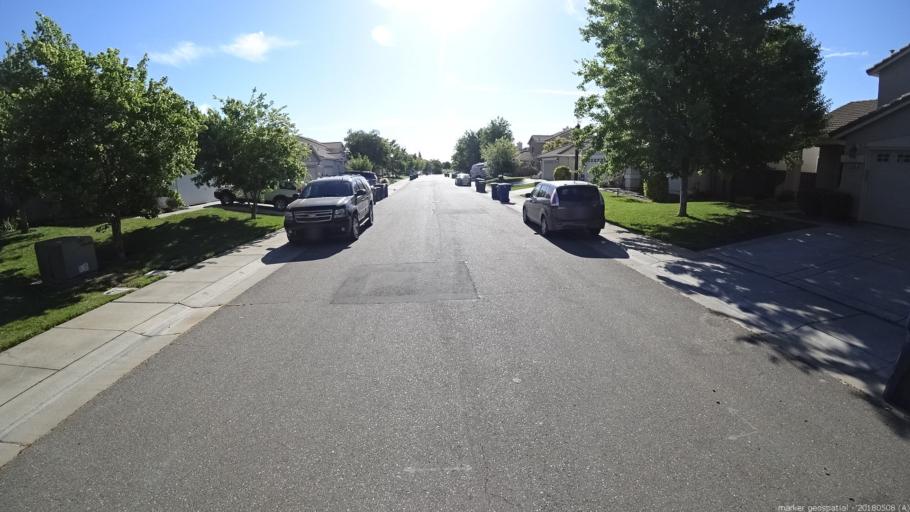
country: US
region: California
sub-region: Sacramento County
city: Elverta
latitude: 38.6759
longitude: -121.5065
